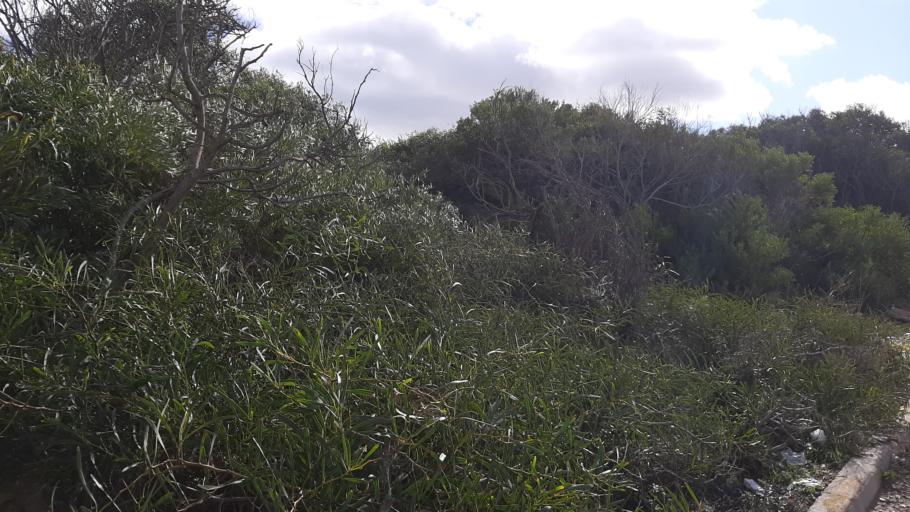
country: TN
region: Tunis
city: Al Marsa
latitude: 36.9193
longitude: 10.3023
